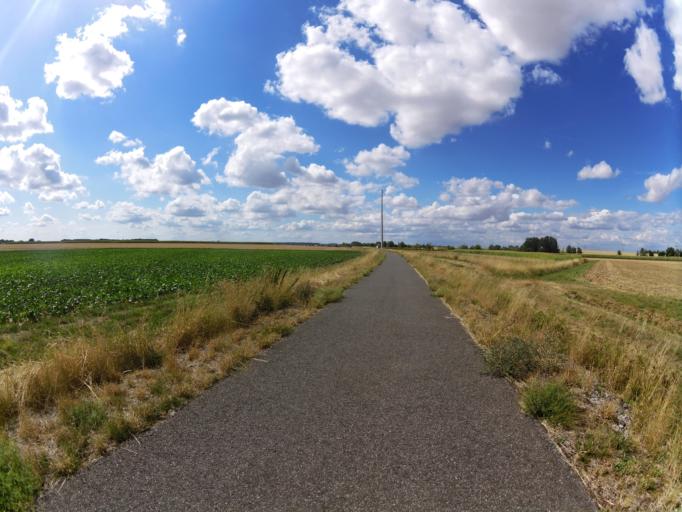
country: DE
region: Bavaria
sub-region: Regierungsbezirk Unterfranken
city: Aub
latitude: 49.5651
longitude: 10.0451
